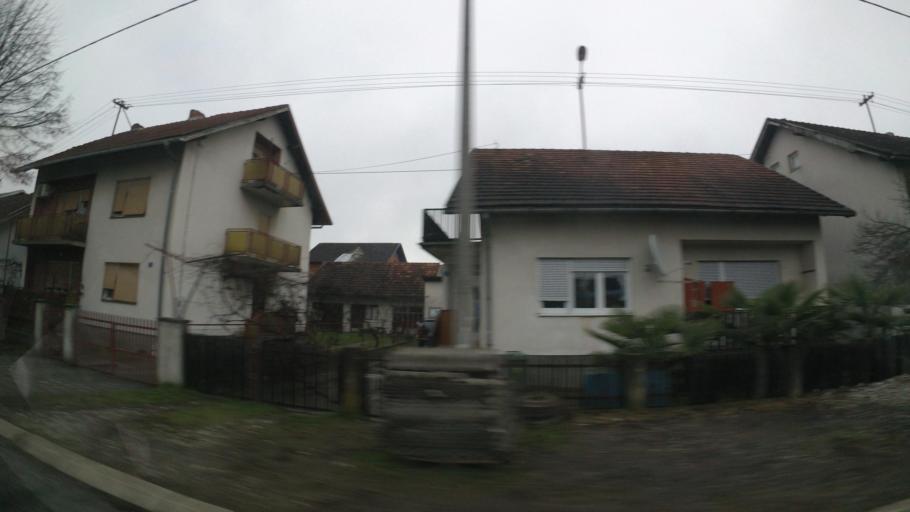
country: HR
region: Sisacko-Moslavacka
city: Glina
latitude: 45.3386
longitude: 16.0941
